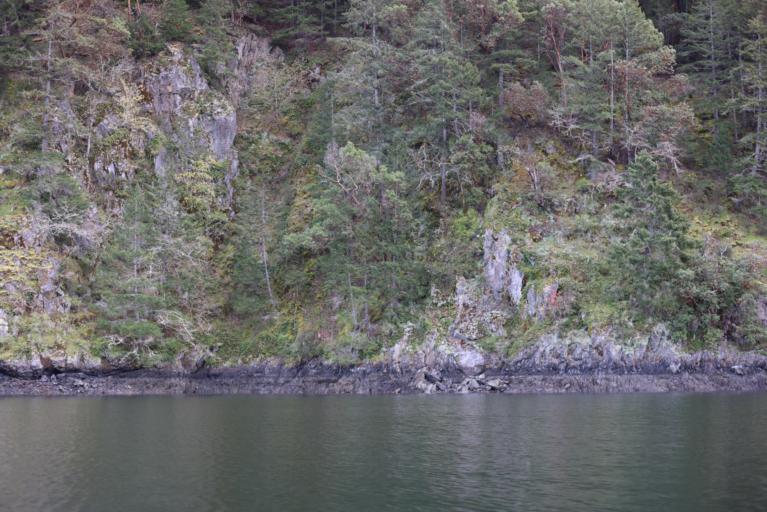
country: CA
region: British Columbia
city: Langford
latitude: 48.5174
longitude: -123.5361
